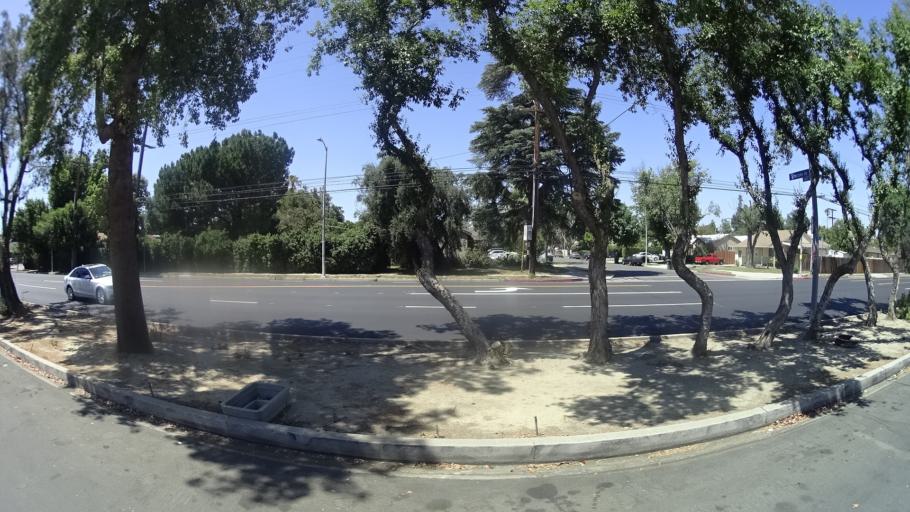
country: US
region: California
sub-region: Los Angeles County
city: Northridge
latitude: 34.1937
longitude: -118.5165
